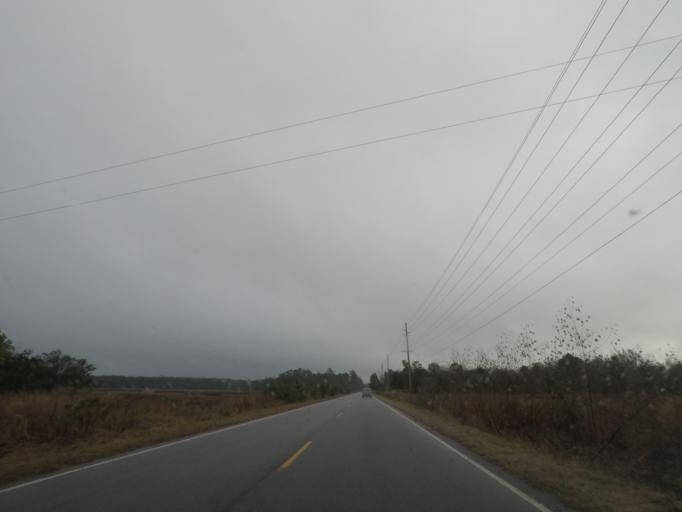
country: US
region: South Carolina
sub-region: Charleston County
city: Meggett
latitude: 32.6702
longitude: -80.3451
